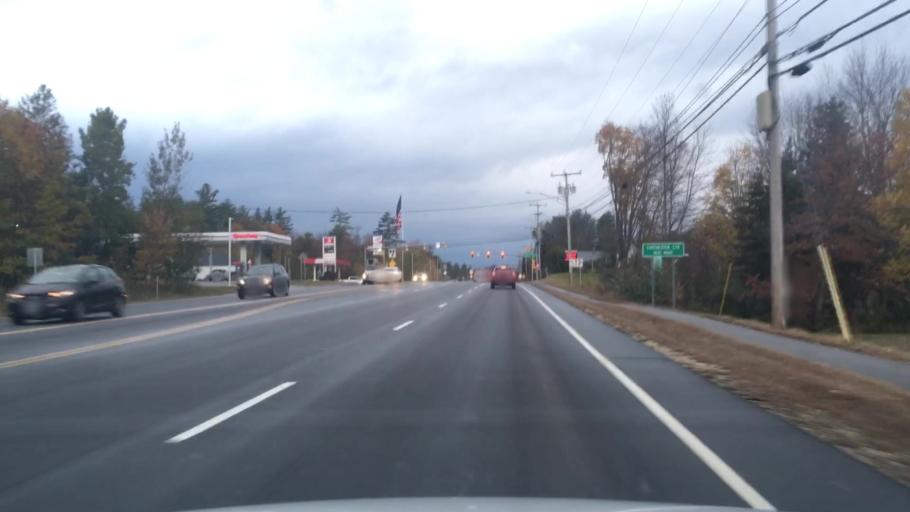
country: US
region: New Hampshire
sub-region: Merrimack County
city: Chichester
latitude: 43.2432
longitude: -71.4026
